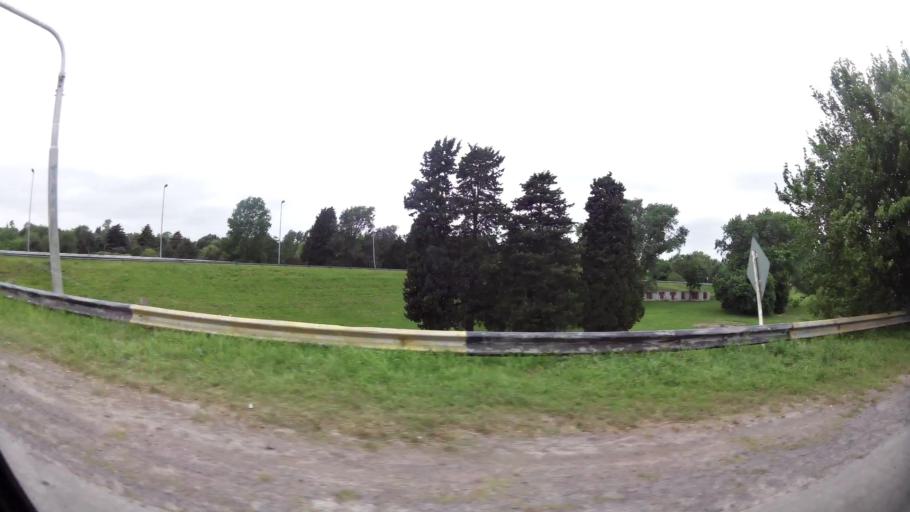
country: AR
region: Buenos Aires
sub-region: Partido de La Plata
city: La Plata
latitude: -35.0352
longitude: -58.0920
